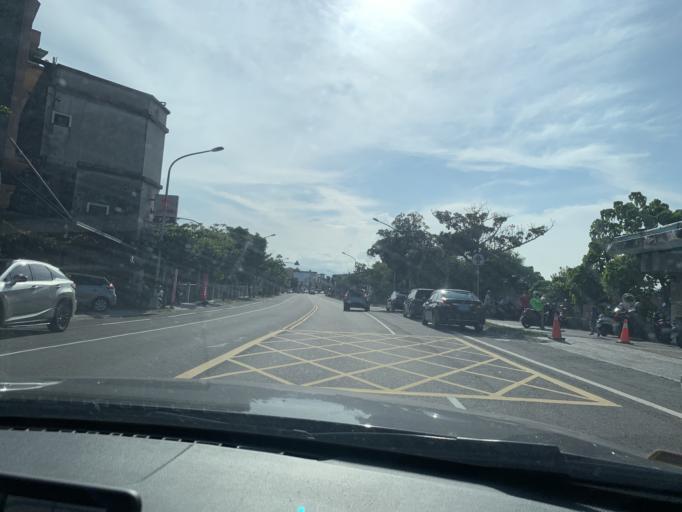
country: TW
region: Taiwan
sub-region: Yilan
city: Yilan
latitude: 24.6686
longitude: 121.8236
